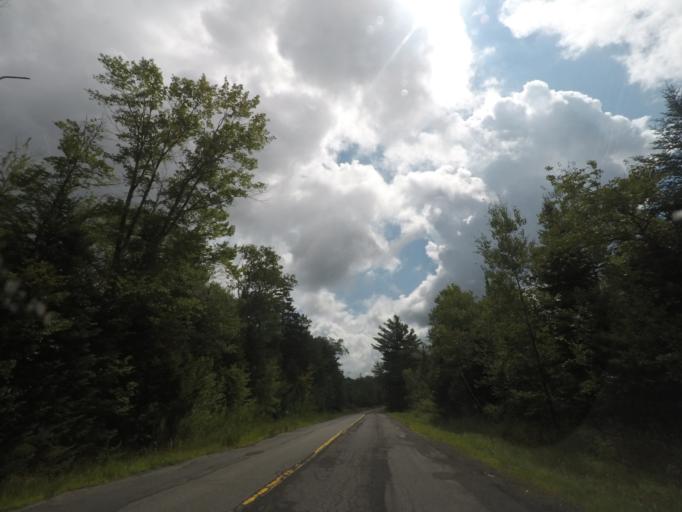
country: US
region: New York
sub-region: Rensselaer County
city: Poestenkill
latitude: 42.6873
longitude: -73.4349
